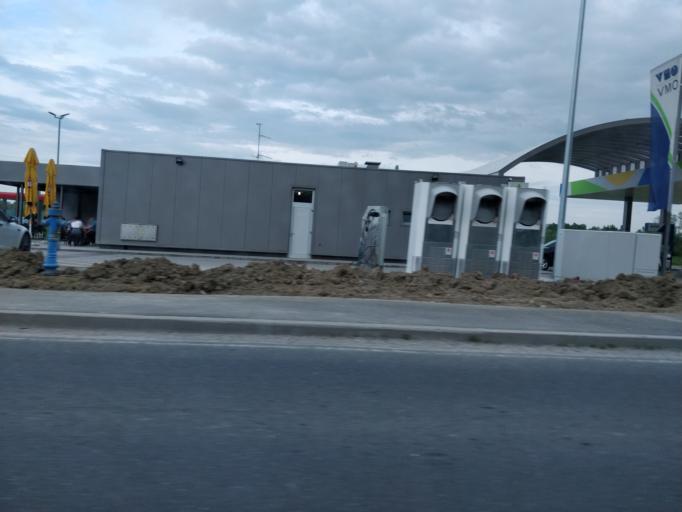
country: HR
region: Zagrebacka
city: Brckovljani
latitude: 45.7670
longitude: 16.2334
